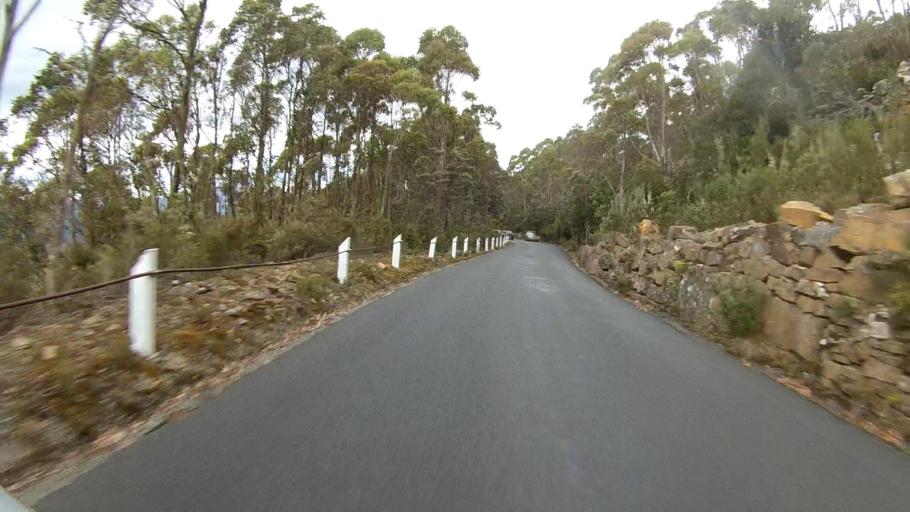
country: AU
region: Tasmania
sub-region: Glenorchy
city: West Moonah
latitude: -42.8988
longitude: 147.2440
